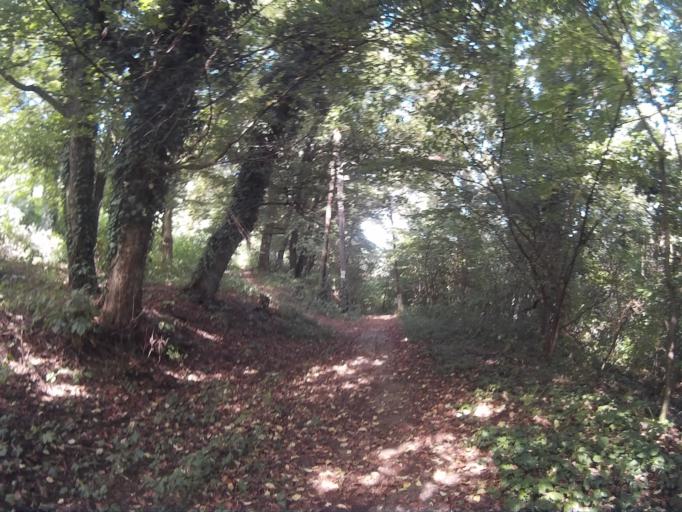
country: HU
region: Vas
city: Koszeg
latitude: 47.4002
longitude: 16.5327
